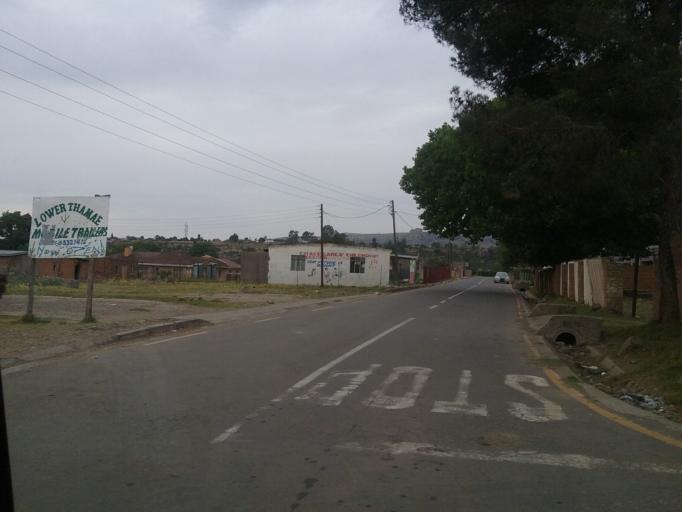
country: LS
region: Maseru
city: Maseru
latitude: -29.3183
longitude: 27.5103
